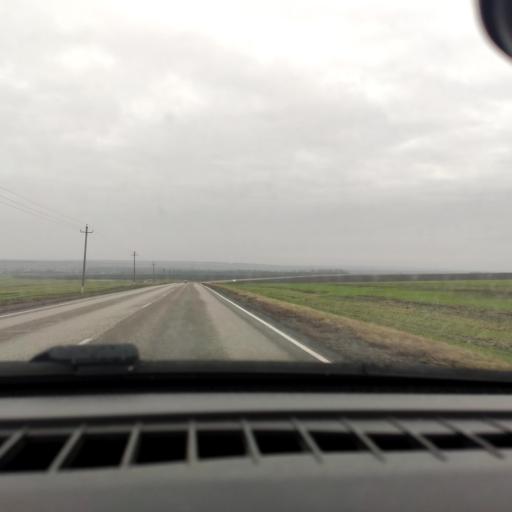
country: RU
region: Belgorod
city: Ilovka
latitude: 50.7770
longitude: 38.7901
